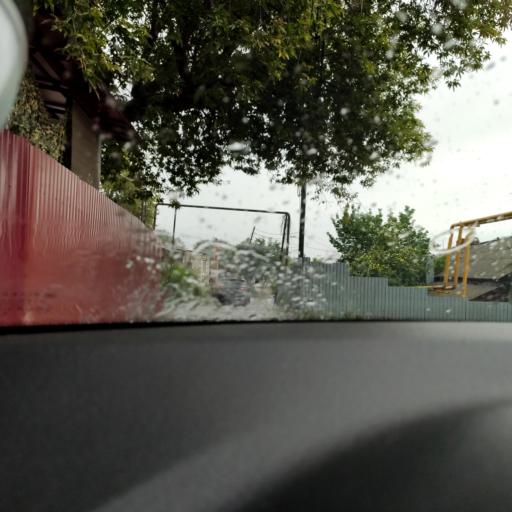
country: RU
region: Samara
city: Samara
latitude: 53.1749
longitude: 50.1546
